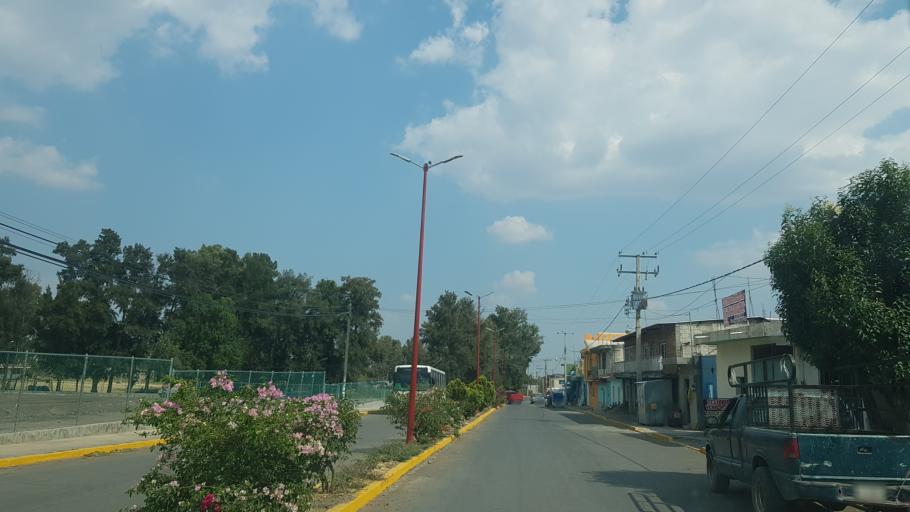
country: MX
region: Puebla
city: San Juan Amecac
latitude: 18.8308
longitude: -98.6590
